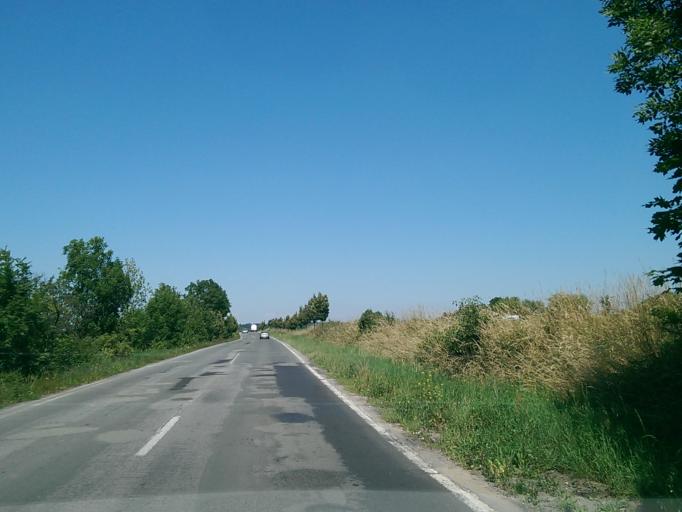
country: CZ
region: Central Bohemia
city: Benatky nad Jizerou
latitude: 50.2955
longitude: 14.8489
